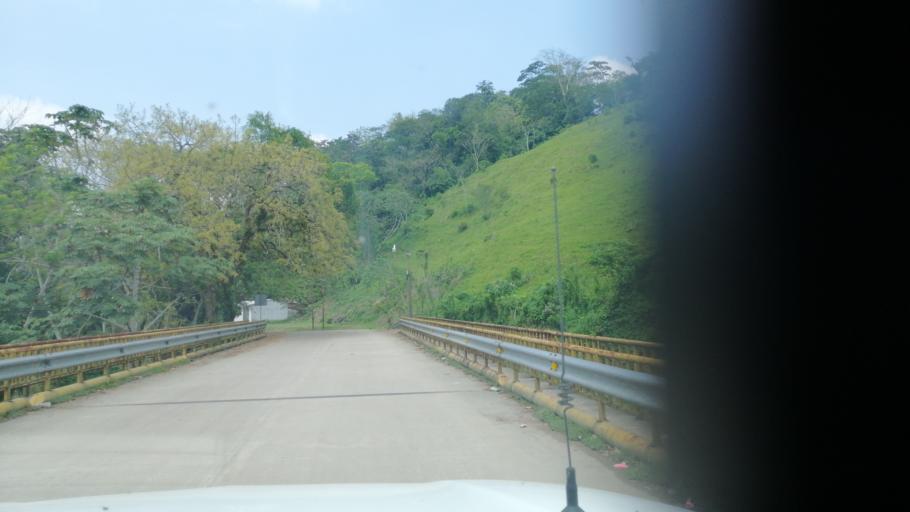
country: MX
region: Chiapas
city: Ostuacan
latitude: 17.4023
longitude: -93.3331
